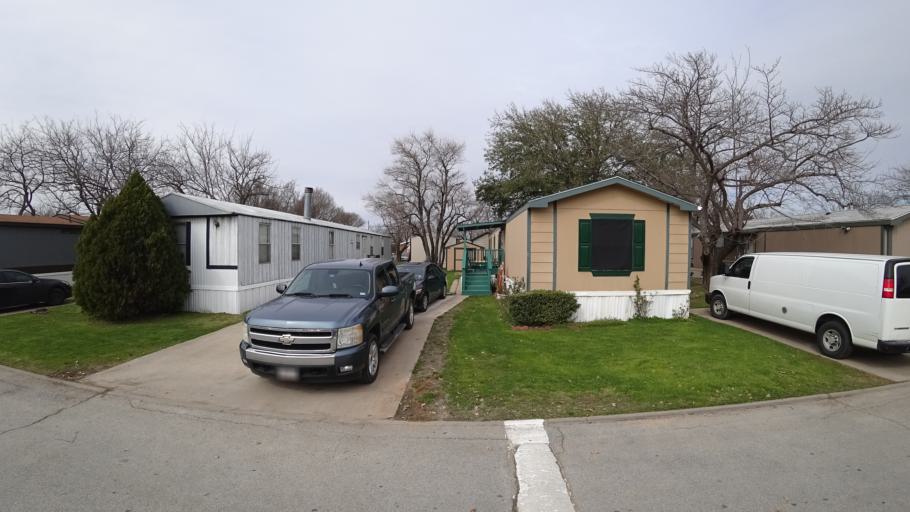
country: US
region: Texas
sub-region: Denton County
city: Lewisville
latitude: 33.0342
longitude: -96.9893
